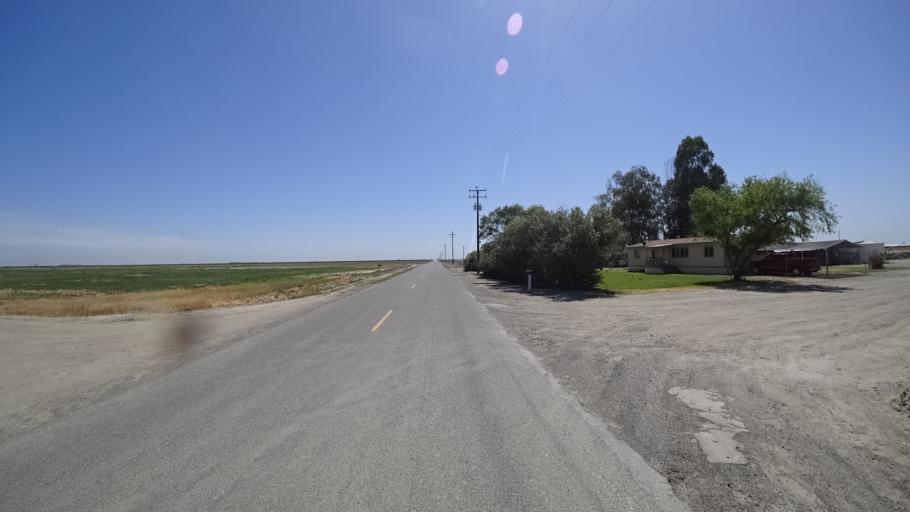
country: US
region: California
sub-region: Kings County
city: Stratford
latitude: 36.1893
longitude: -119.7536
